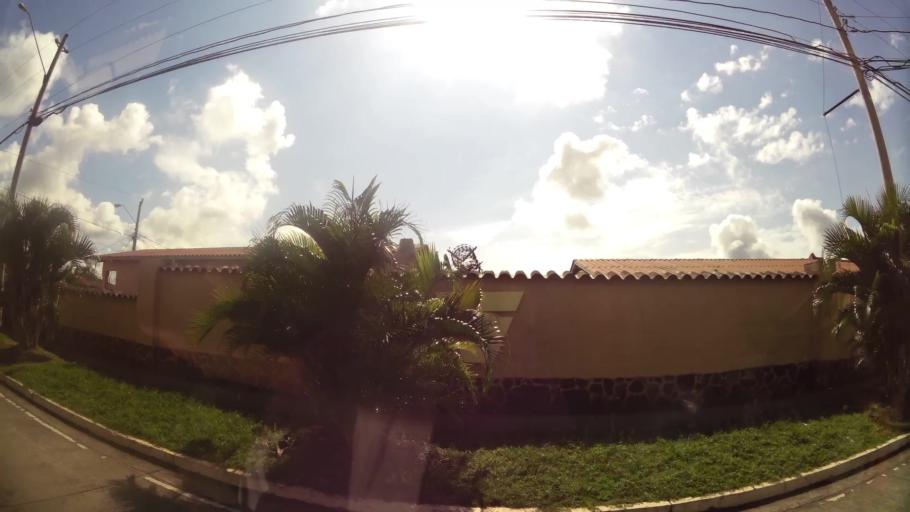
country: PA
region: Panama
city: Nuevo Arraijan
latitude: 8.9034
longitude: -79.7447
